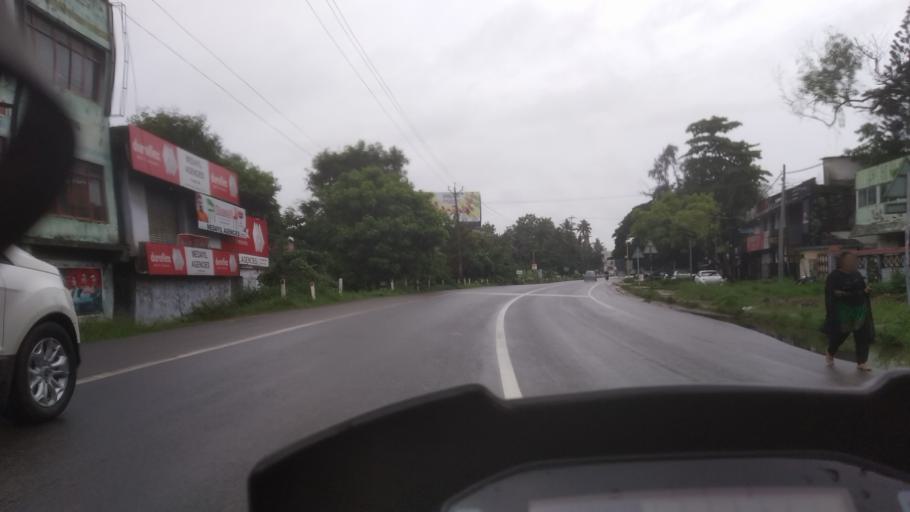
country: IN
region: Kerala
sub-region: Alappuzha
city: Kayankulam
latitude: 9.1379
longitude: 76.5123
